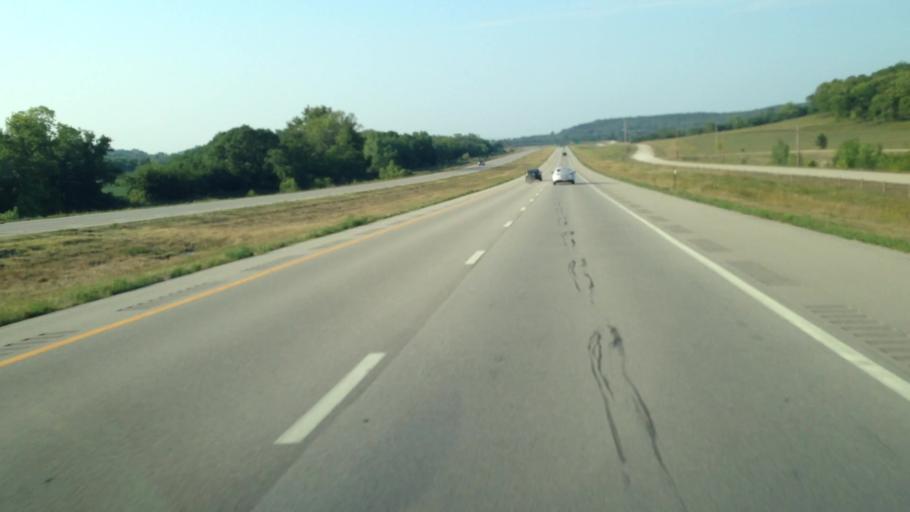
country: US
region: Kansas
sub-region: Douglas County
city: Baldwin City
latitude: 38.8566
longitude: -95.2618
